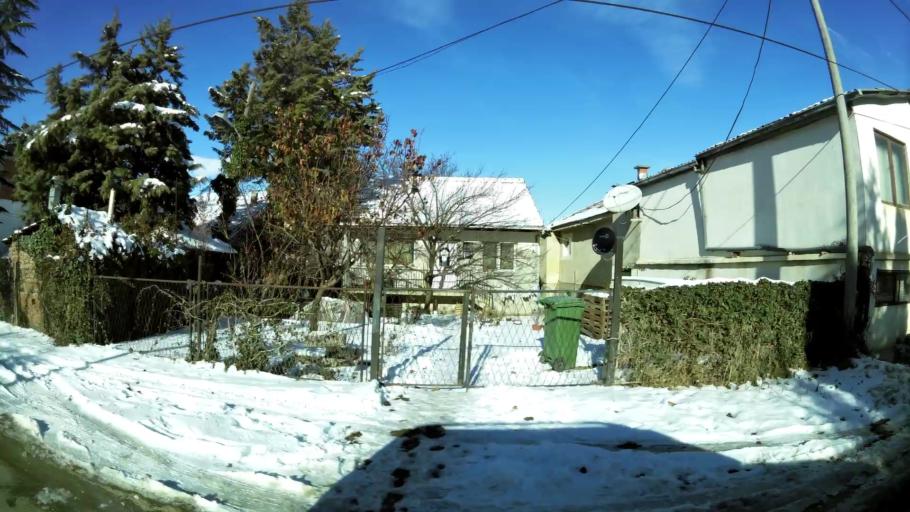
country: MK
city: Grchec
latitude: 41.9767
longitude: 21.3129
